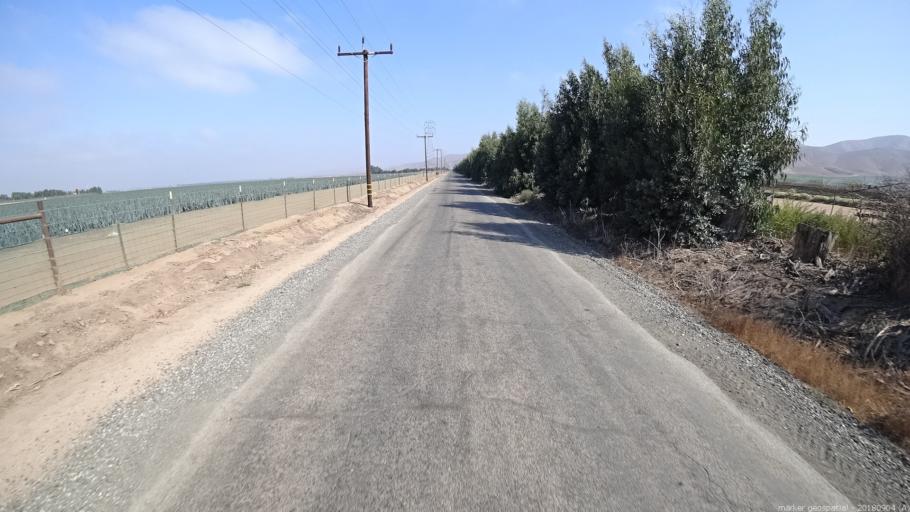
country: US
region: California
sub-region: Monterey County
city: Soledad
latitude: 36.4481
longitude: -121.3318
